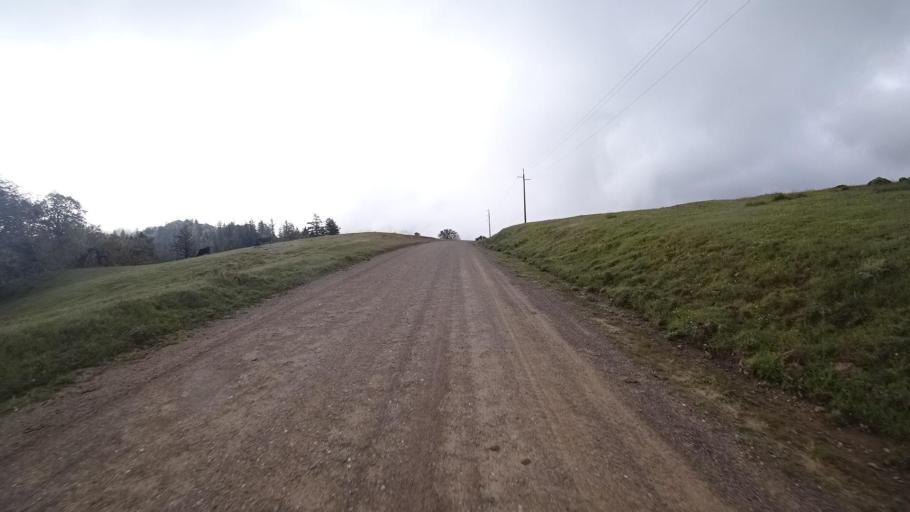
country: US
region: California
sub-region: Humboldt County
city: Redway
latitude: 40.2075
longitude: -123.7296
